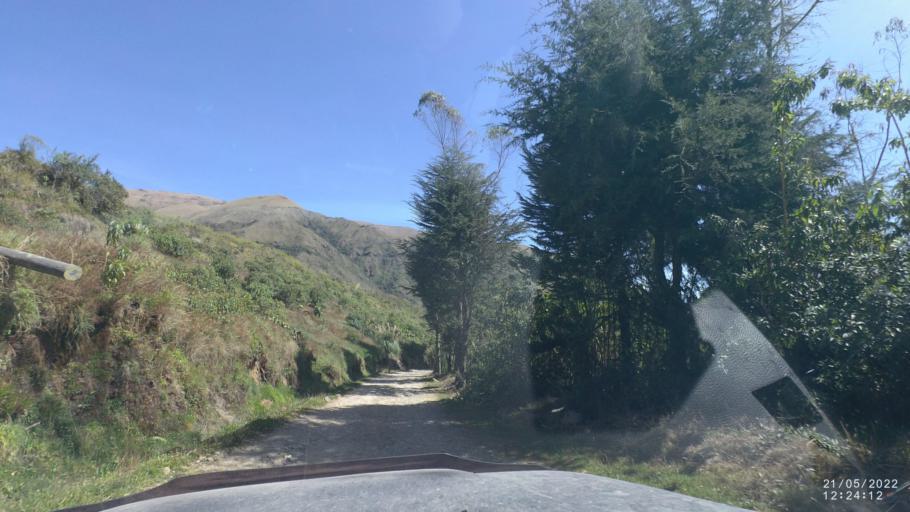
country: BO
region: Cochabamba
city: Colomi
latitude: -17.2206
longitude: -65.9059
